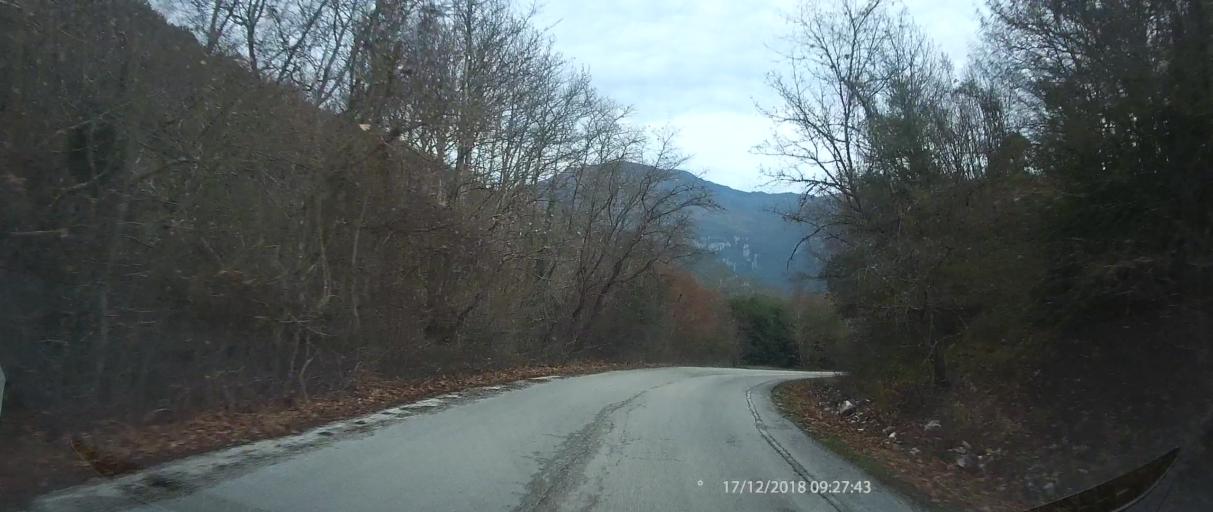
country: GR
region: Epirus
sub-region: Nomos Ioanninon
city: Kalpaki
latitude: 39.9432
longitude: 20.6815
